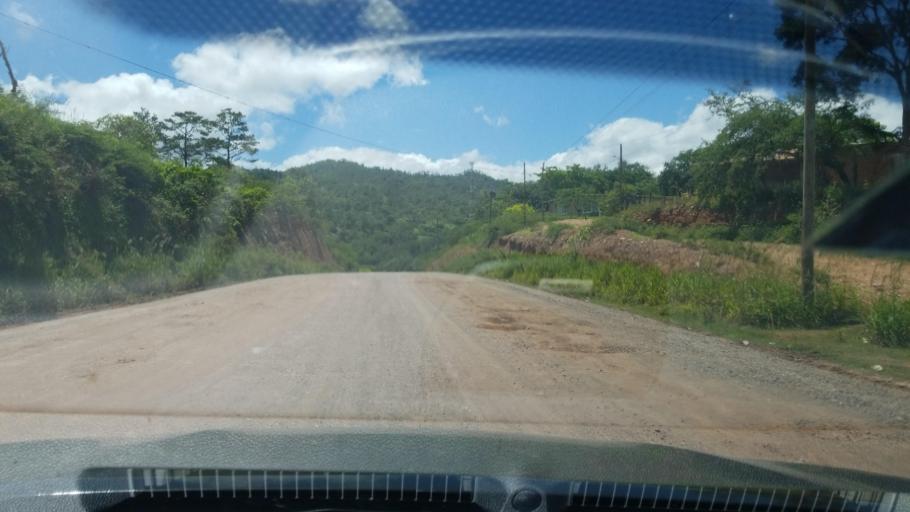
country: HN
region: Francisco Morazan
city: San Juan de Flores
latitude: 14.3368
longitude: -87.0461
